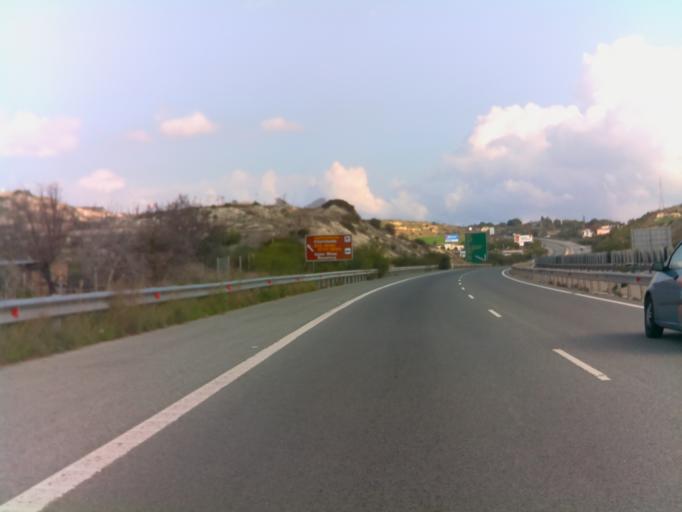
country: CY
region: Larnaka
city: Kofinou
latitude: 34.7913
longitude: 33.3444
